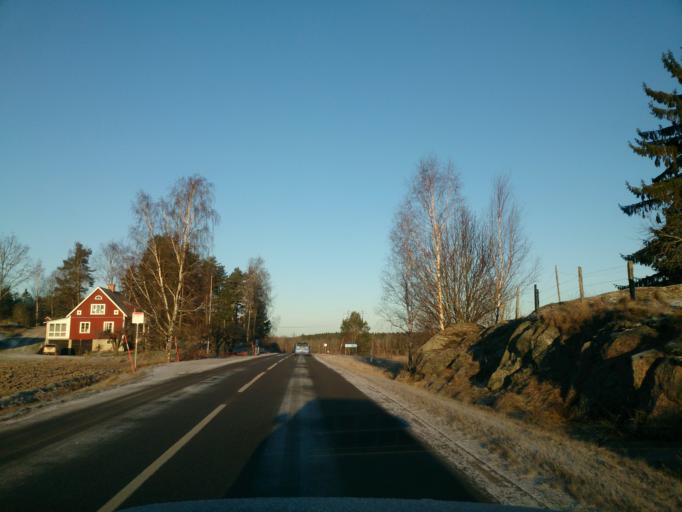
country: SE
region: OEstergoetland
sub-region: Norrkopings Kommun
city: Kimstad
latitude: 58.3802
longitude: 16.0225
